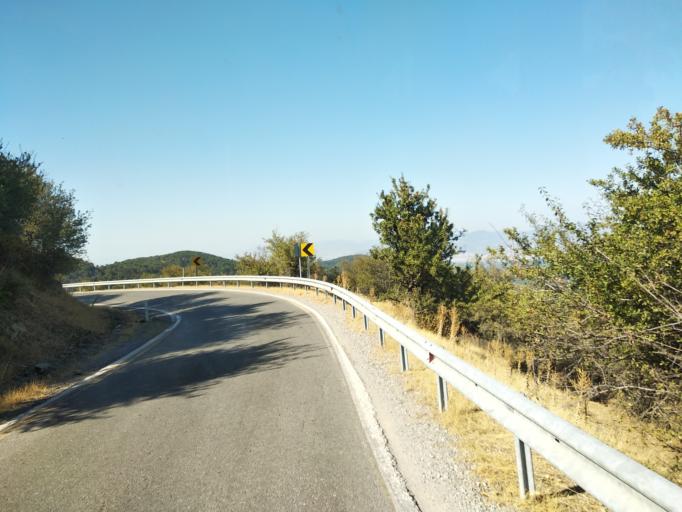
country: TR
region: Izmir
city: Gaziemir
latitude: 38.3237
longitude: 27.0071
